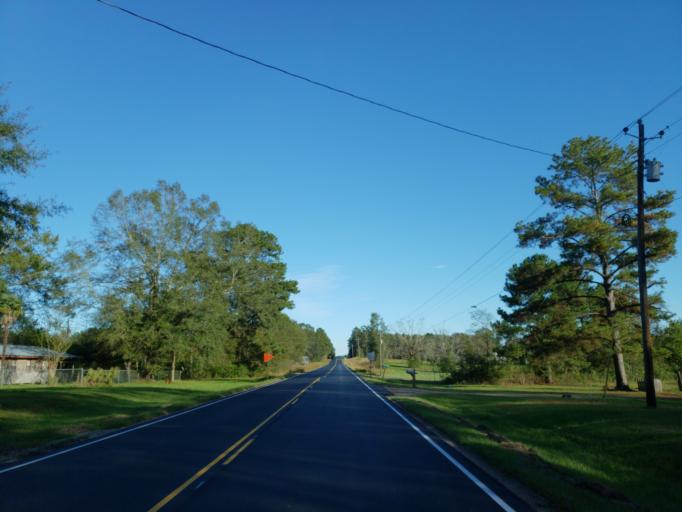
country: US
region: Mississippi
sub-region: Perry County
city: Richton
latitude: 31.3716
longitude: -88.8243
